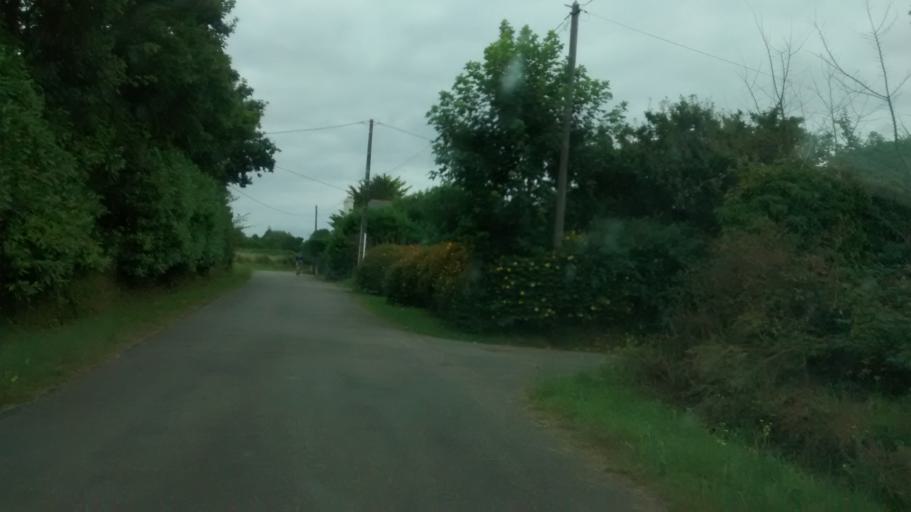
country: FR
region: Brittany
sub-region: Departement du Finistere
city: Lanveoc
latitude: 48.3330
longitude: -4.4334
